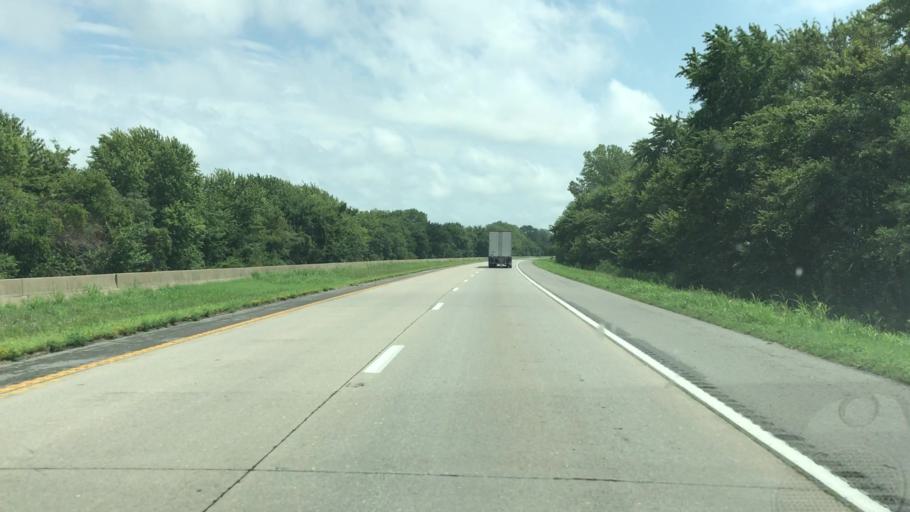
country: US
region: Missouri
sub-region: Pemiscot County
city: Caruthersville
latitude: 36.1314
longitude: -89.6240
